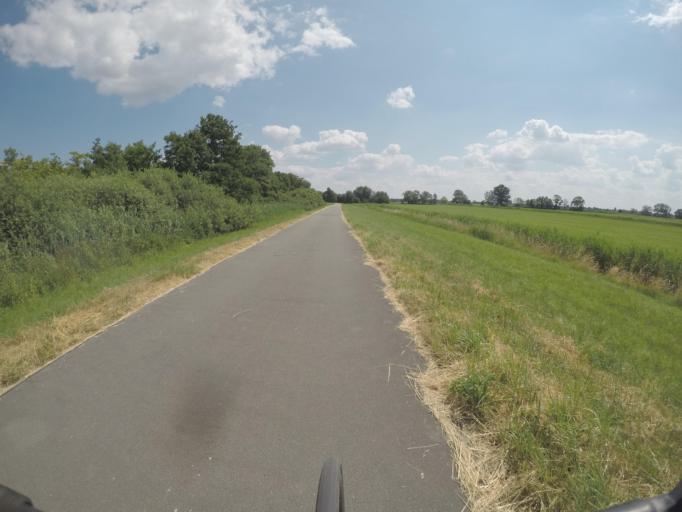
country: DE
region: Brandenburg
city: Roskow
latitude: 52.4399
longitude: 12.6897
